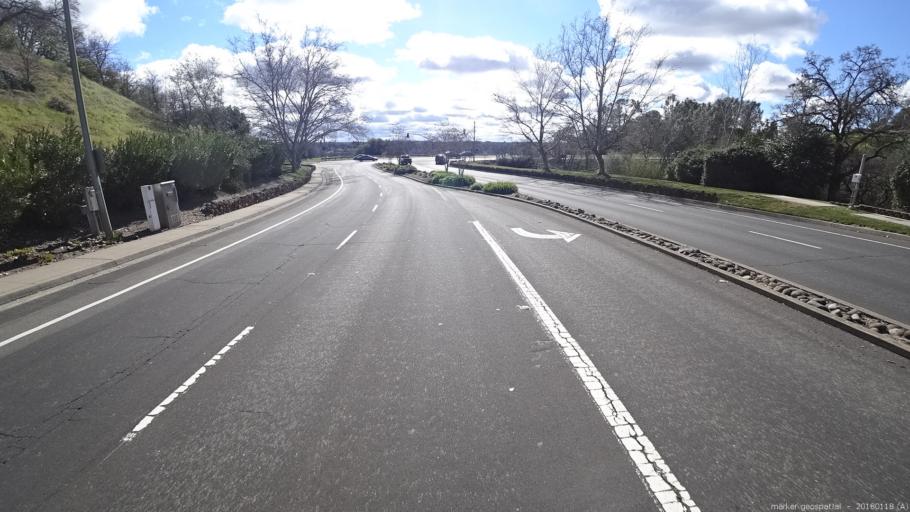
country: US
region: California
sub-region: Sacramento County
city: Folsom
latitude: 38.6801
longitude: -121.1927
